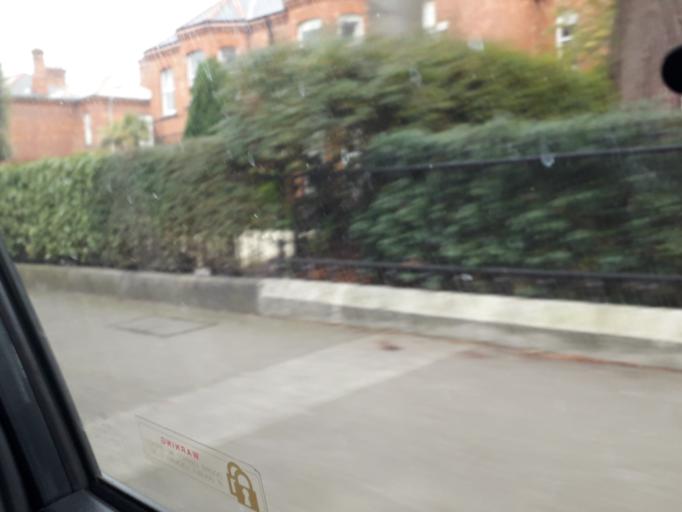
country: IE
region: Leinster
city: Sandymount
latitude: 53.3229
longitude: -6.2115
